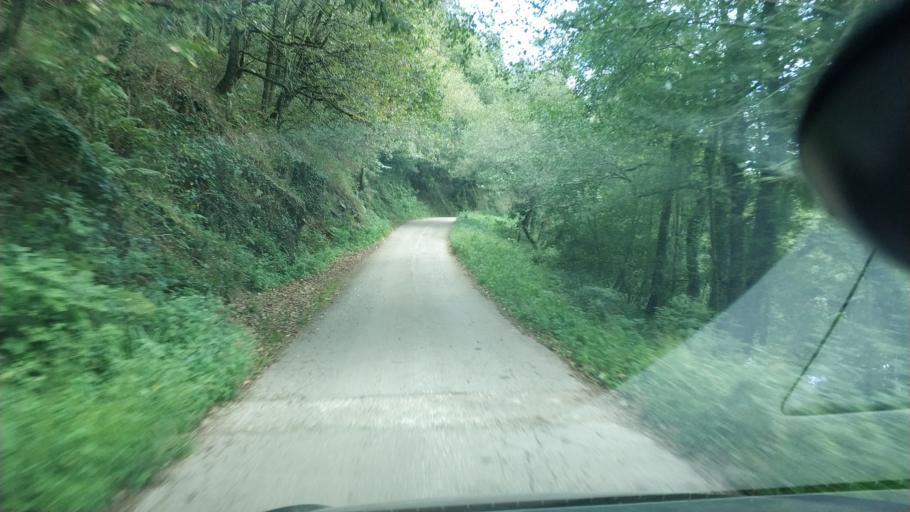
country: ES
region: Cantabria
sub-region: Provincia de Cantabria
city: Santa Maria de Cayon
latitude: 43.2980
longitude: -3.8556
